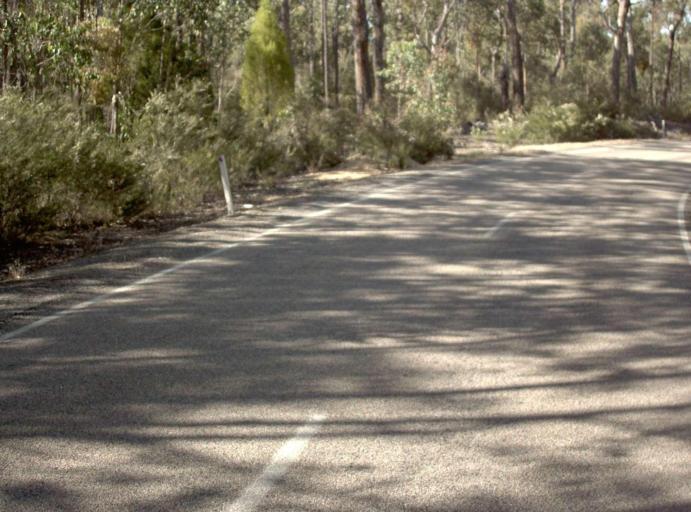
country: AU
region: Victoria
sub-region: East Gippsland
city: Lakes Entrance
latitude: -37.5566
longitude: 148.5590
